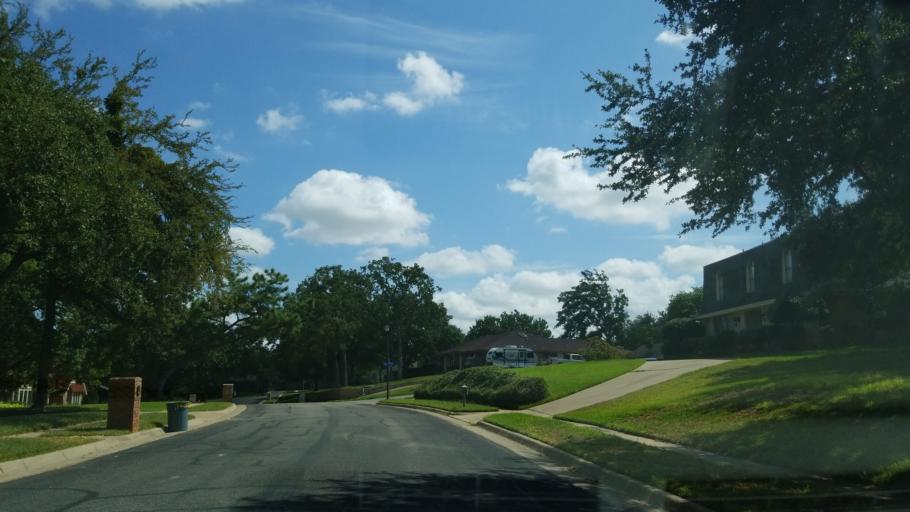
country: US
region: Texas
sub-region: Tarrant County
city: Euless
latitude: 32.8645
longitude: -97.0934
